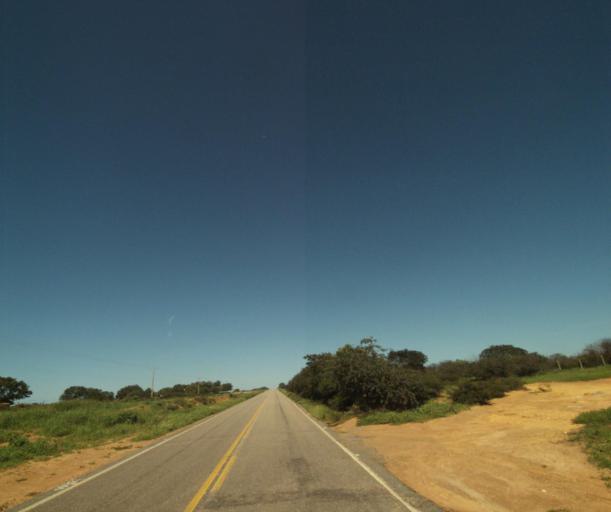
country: BR
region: Bahia
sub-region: Palmas De Monte Alto
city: Palmas de Monte Alto
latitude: -14.2553
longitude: -43.2341
